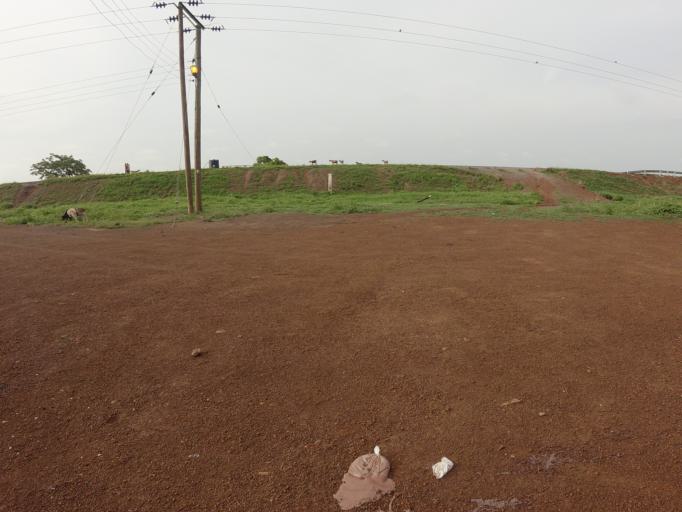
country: GH
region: Northern
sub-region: Yendi
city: Yendi
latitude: 9.9313
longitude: -0.2056
